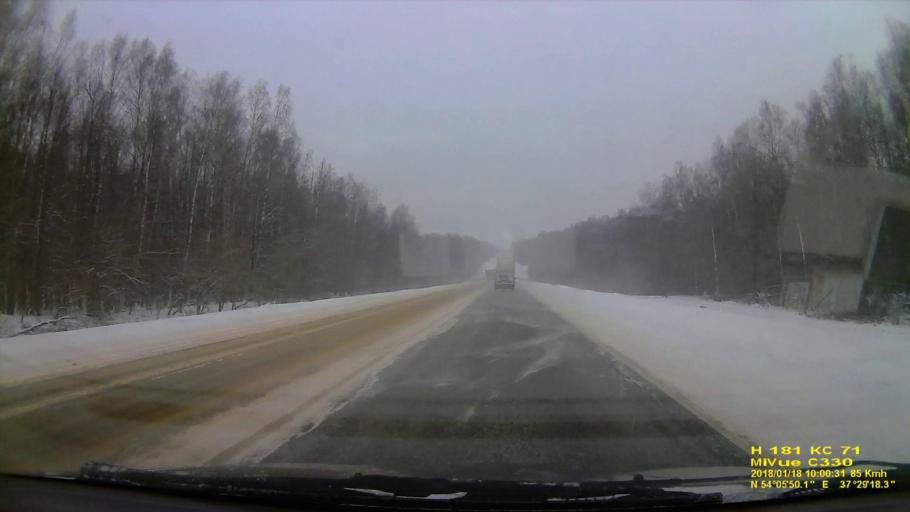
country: RU
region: Tula
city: Pervomayskiy
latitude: 54.0969
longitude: 37.4884
